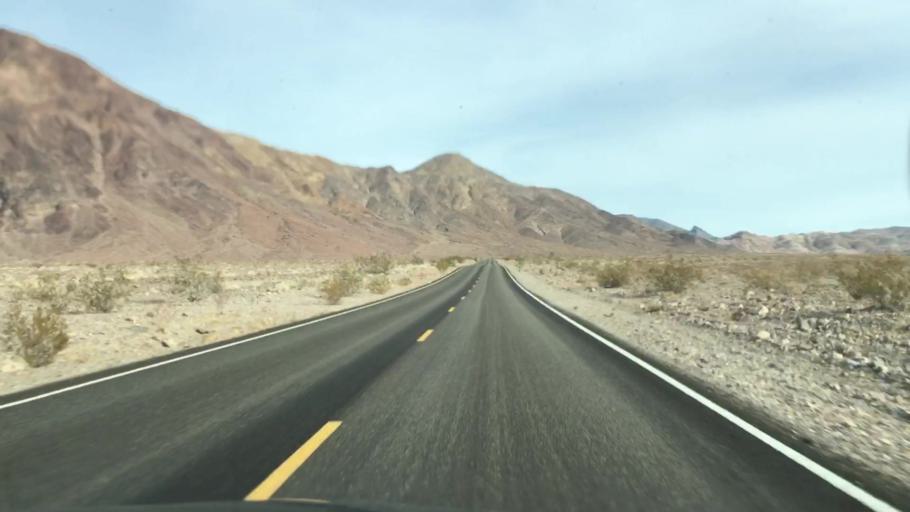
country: US
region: Nevada
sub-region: Nye County
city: Beatty
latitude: 36.6946
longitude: -117.0012
